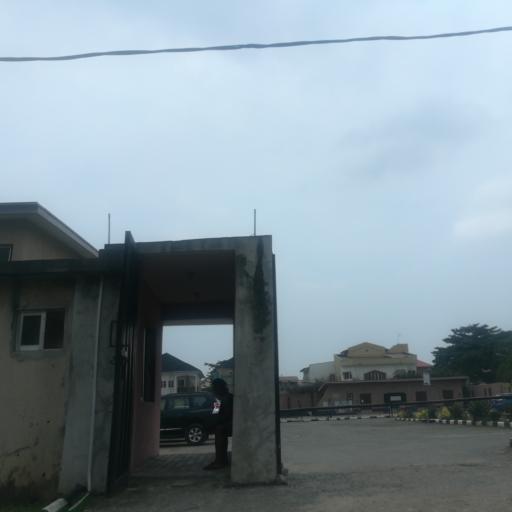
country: NG
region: Lagos
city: Ojota
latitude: 6.5788
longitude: 3.3838
